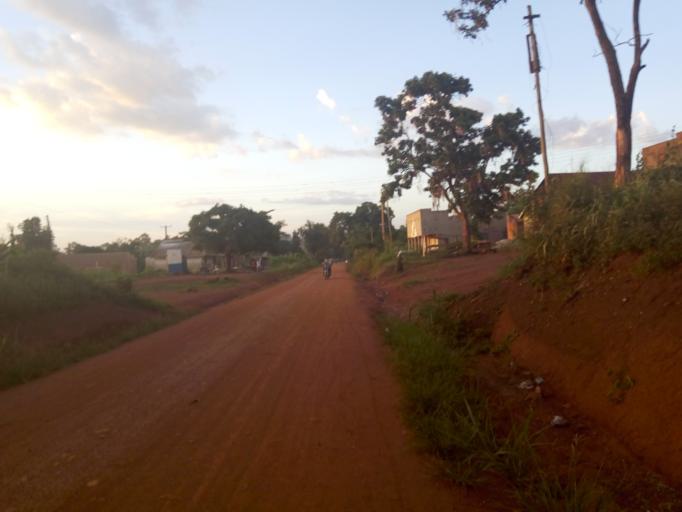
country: UG
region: Western Region
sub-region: Masindi District
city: Masindi
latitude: 1.6738
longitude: 31.7135
